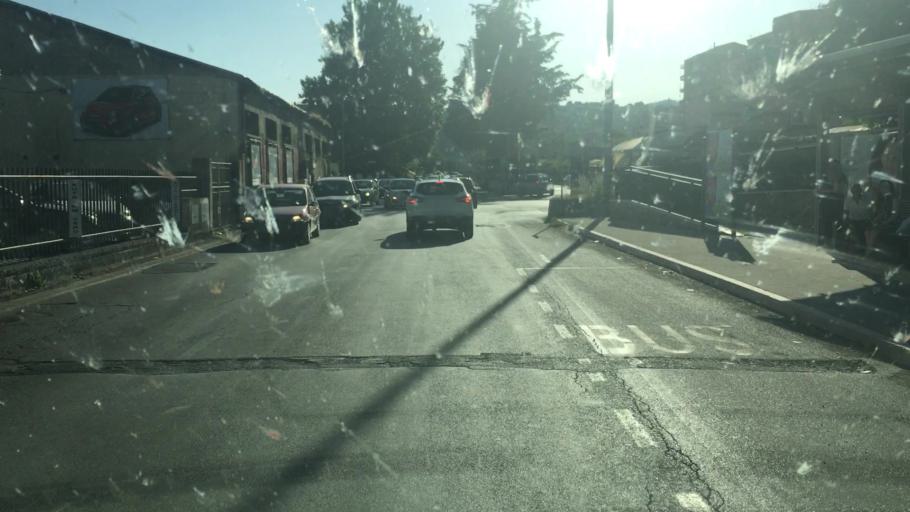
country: IT
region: Basilicate
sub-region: Provincia di Potenza
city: Potenza
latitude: 40.6274
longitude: 15.8027
